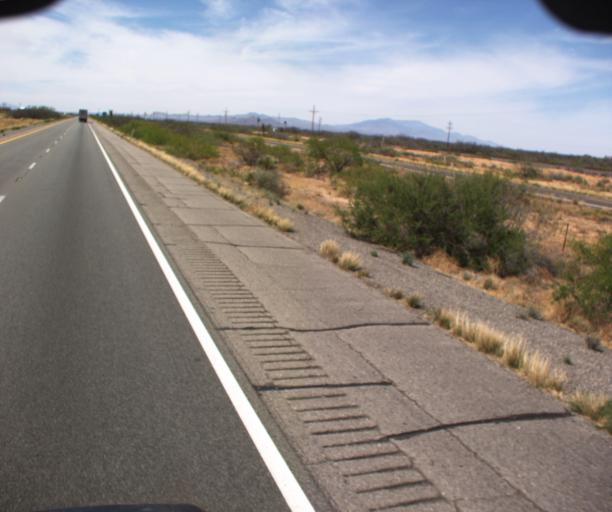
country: US
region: Arizona
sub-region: Cochise County
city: Willcox
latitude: 32.3136
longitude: -109.4245
